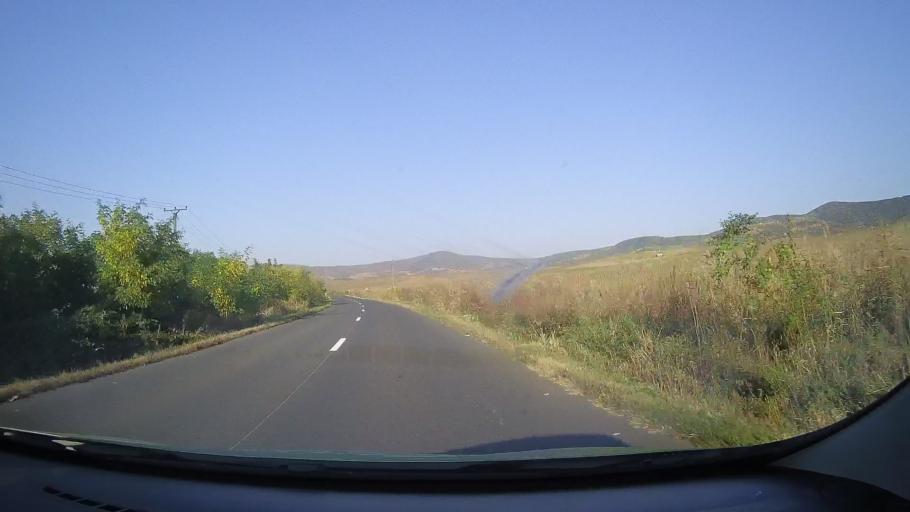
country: RO
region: Arad
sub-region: Comuna Siria
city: Siria
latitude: 46.2276
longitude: 21.6338
